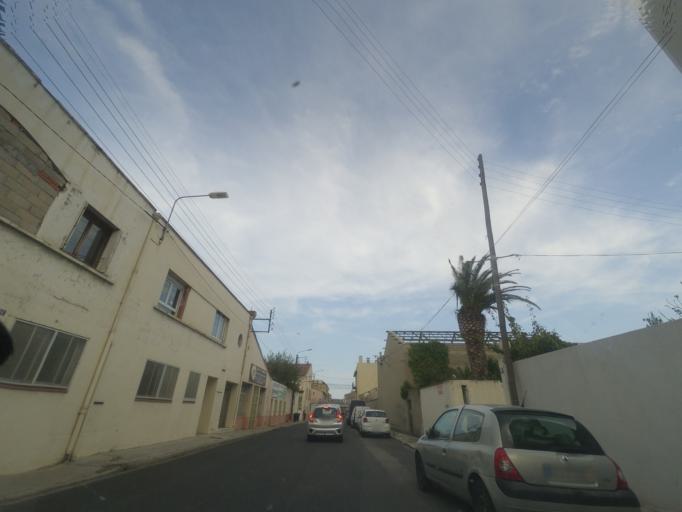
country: FR
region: Languedoc-Roussillon
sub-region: Departement des Pyrenees-Orientales
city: Perpignan
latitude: 42.6987
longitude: 2.8765
